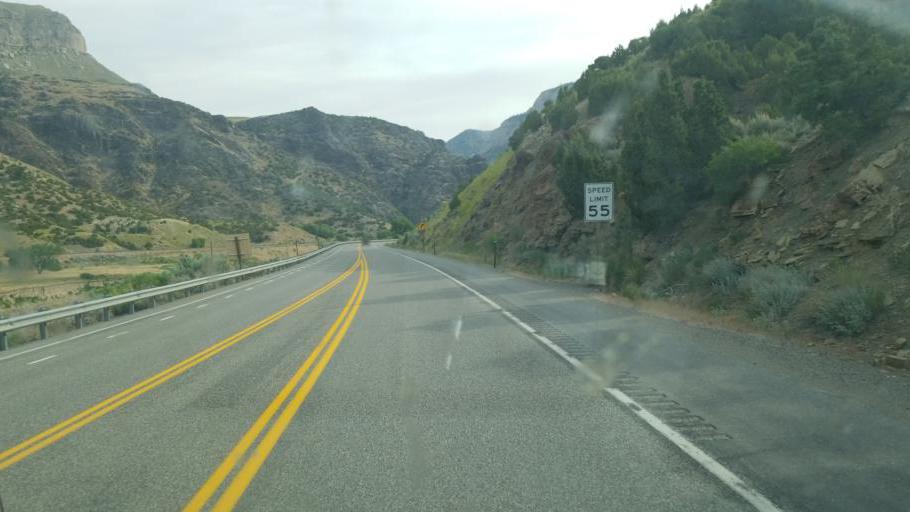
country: US
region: Wyoming
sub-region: Hot Springs County
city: Thermopolis
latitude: 43.4351
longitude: -108.1762
